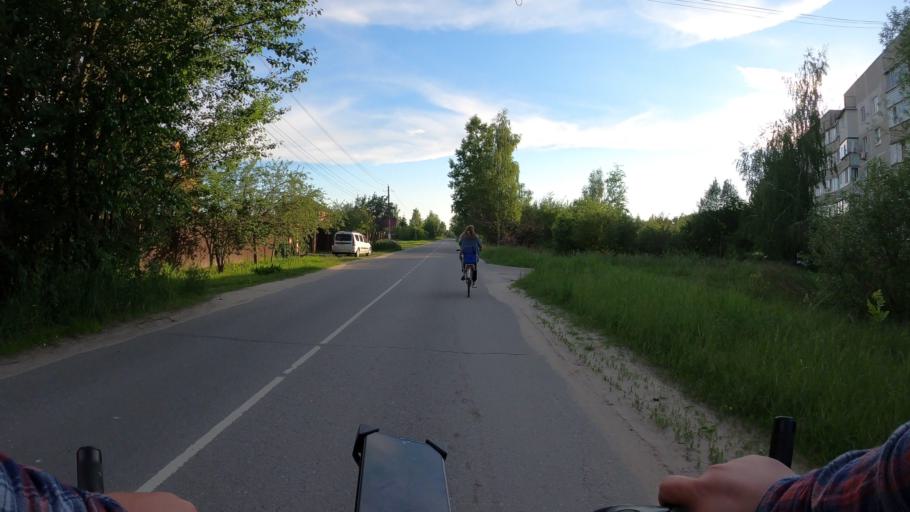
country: RU
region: Moskovskaya
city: Ashitkovo
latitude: 55.4339
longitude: 38.5816
